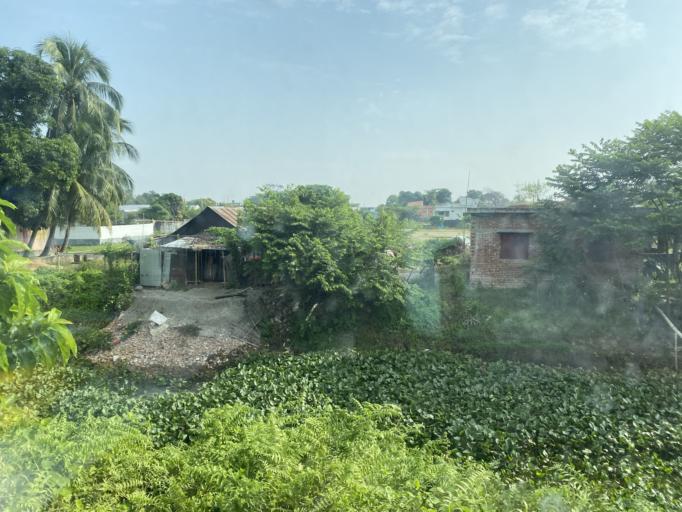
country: BD
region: Chittagong
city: Nabinagar
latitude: 23.9607
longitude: 91.1188
